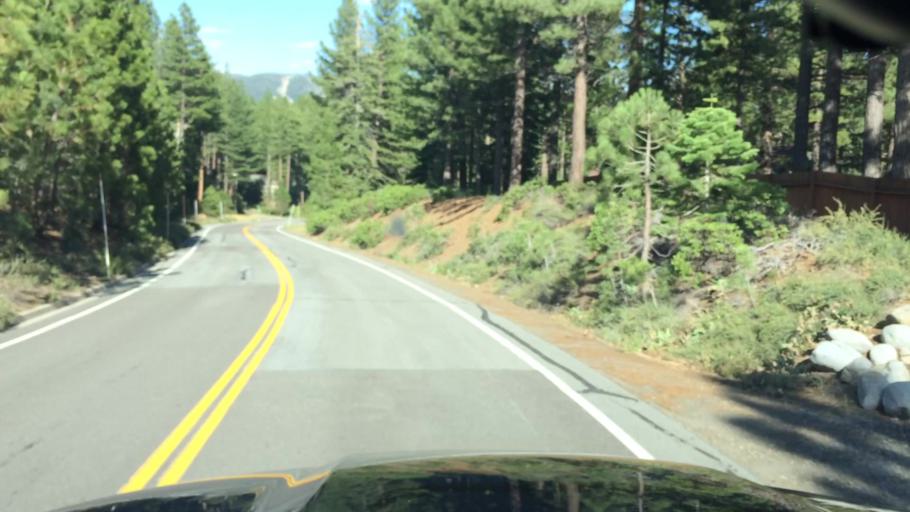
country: US
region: Nevada
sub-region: Washoe County
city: Incline Village
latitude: 39.2551
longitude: -119.9629
